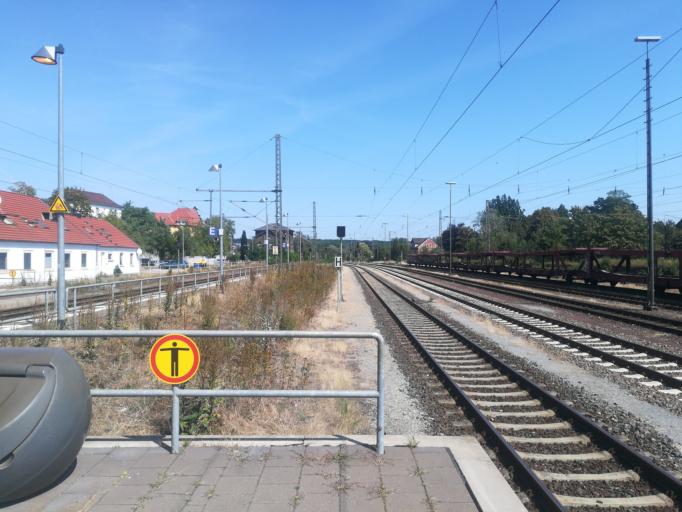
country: DE
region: Lower Saxony
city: Helmstedt
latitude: 52.2224
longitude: 11.0115
